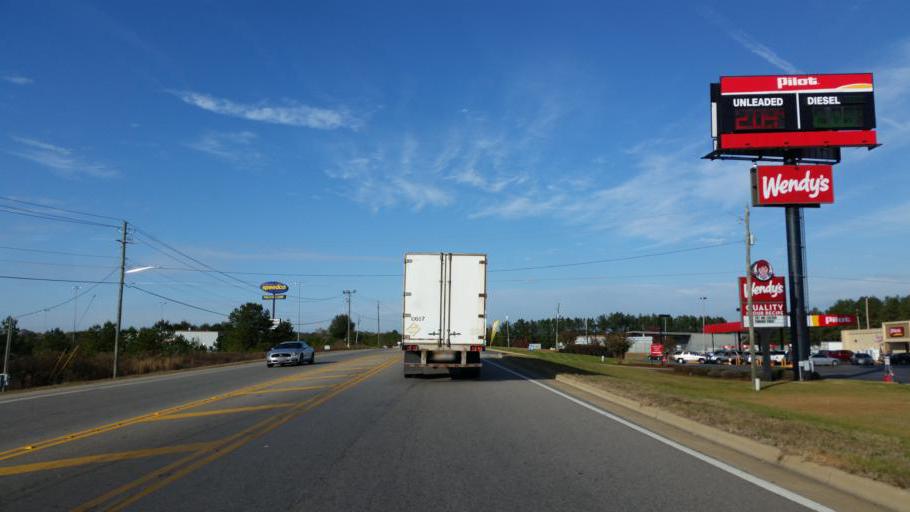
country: US
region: Alabama
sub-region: Tuscaloosa County
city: Holt
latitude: 33.1779
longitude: -87.4474
